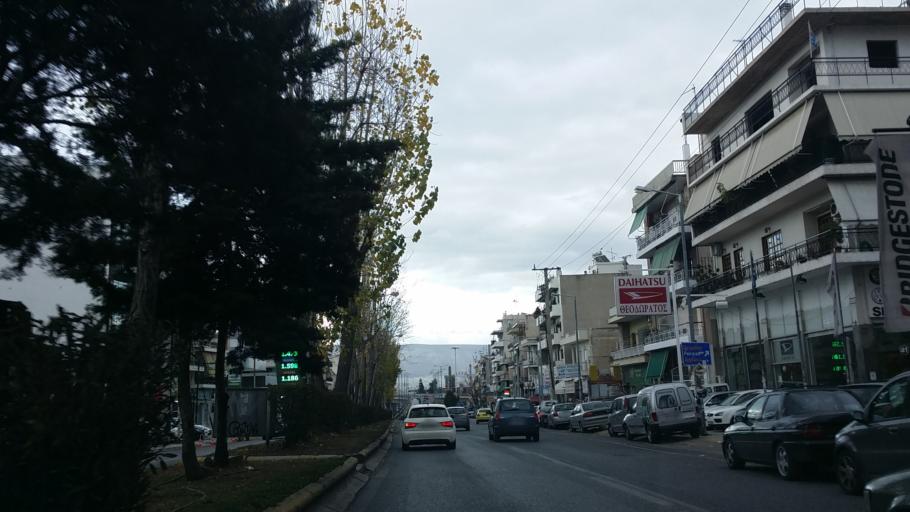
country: GR
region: Attica
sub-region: Nomarchia Athinas
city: Agia Varvara
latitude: 37.9775
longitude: 23.6634
